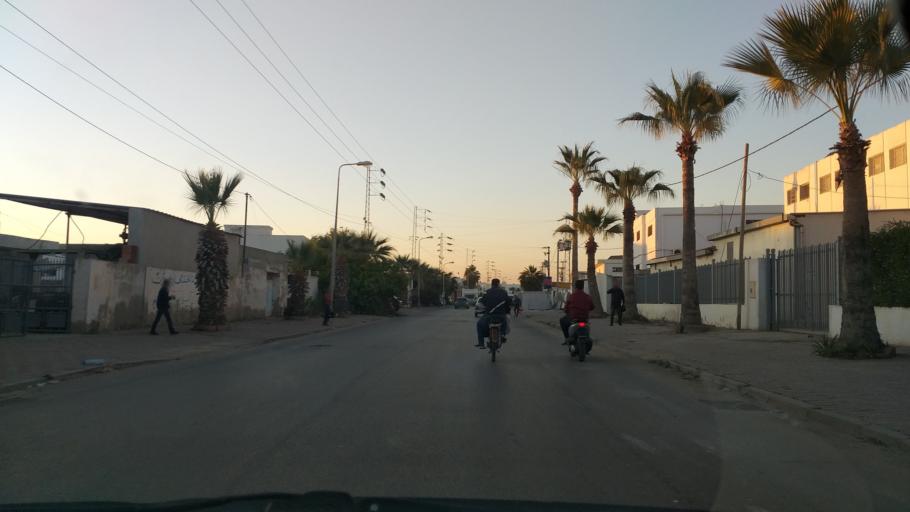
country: TN
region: Safaqis
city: Al Qarmadah
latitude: 34.7612
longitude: 10.7783
